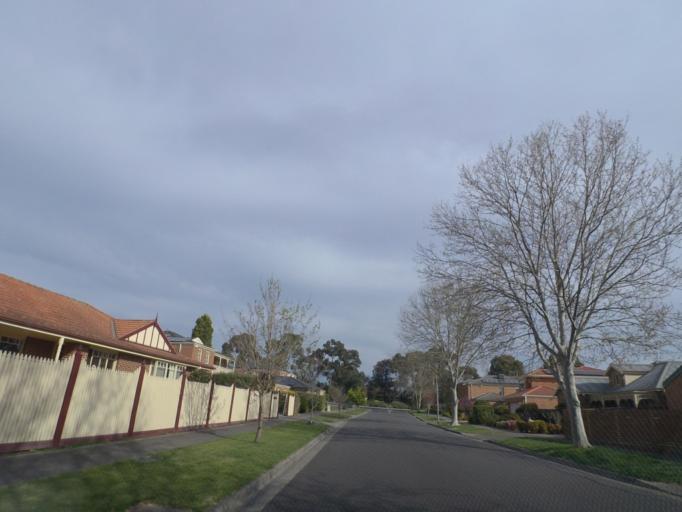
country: AU
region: Victoria
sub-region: Knox
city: Wantirna South
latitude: -37.8759
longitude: 145.2287
